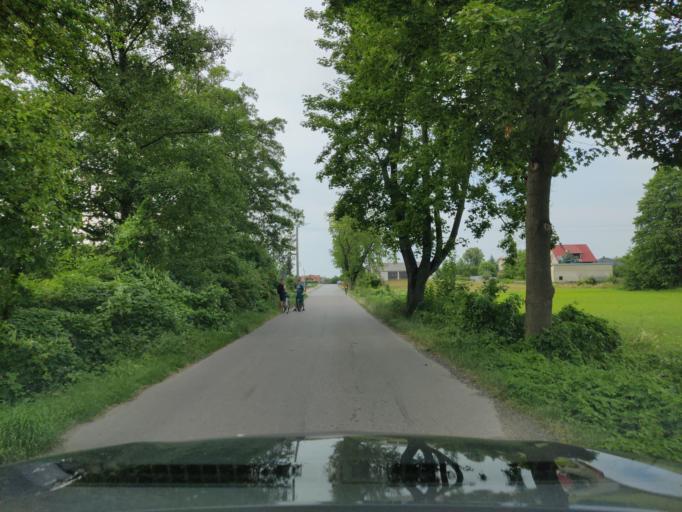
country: PL
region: Masovian Voivodeship
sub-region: Powiat pultuski
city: Obryte
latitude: 52.7128
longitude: 21.2420
